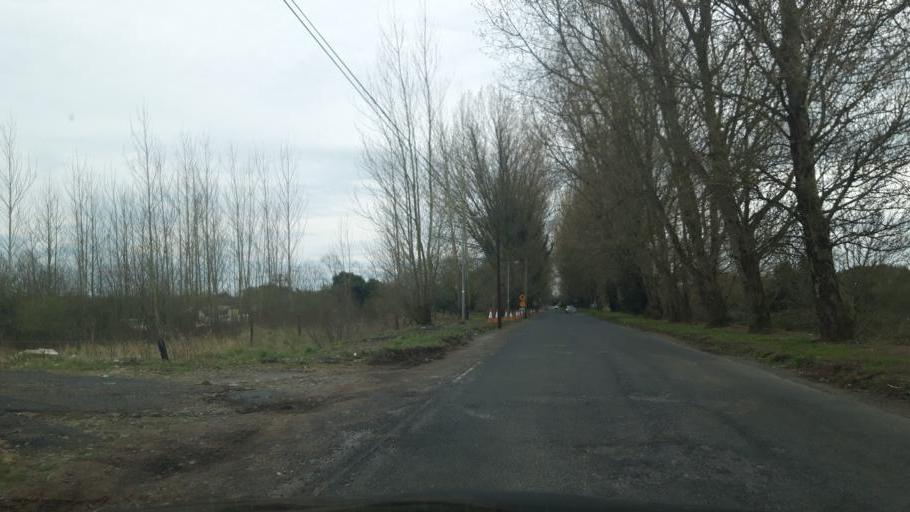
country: IE
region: Leinster
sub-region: Uibh Fhaili
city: Edenderry
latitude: 53.3326
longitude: -7.0395
